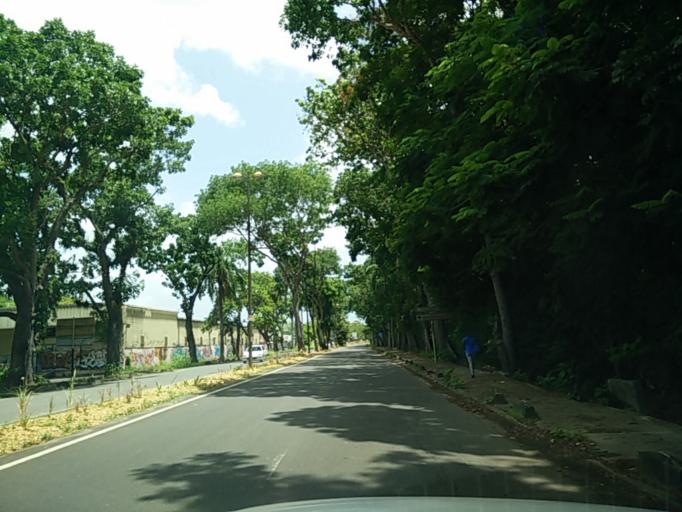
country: GP
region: Guadeloupe
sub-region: Guadeloupe
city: Pointe-a-Pitre
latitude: 16.2576
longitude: -61.5218
